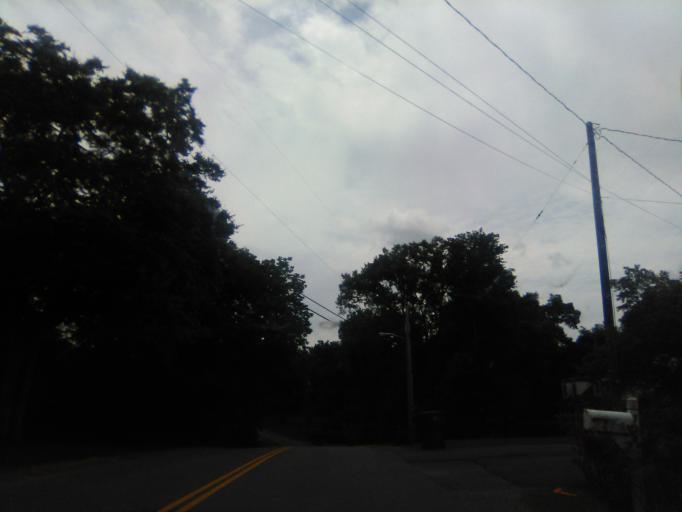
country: US
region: Tennessee
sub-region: Davidson County
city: Belle Meade
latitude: 36.1191
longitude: -86.8801
